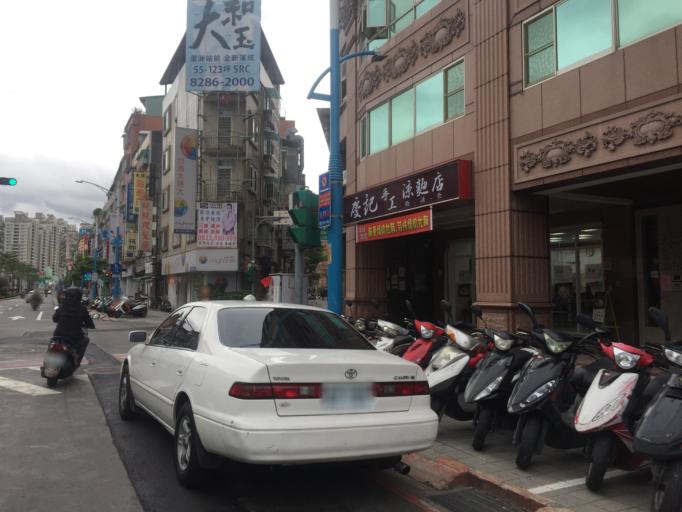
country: TW
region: Taipei
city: Taipei
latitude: 25.0873
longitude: 121.4712
